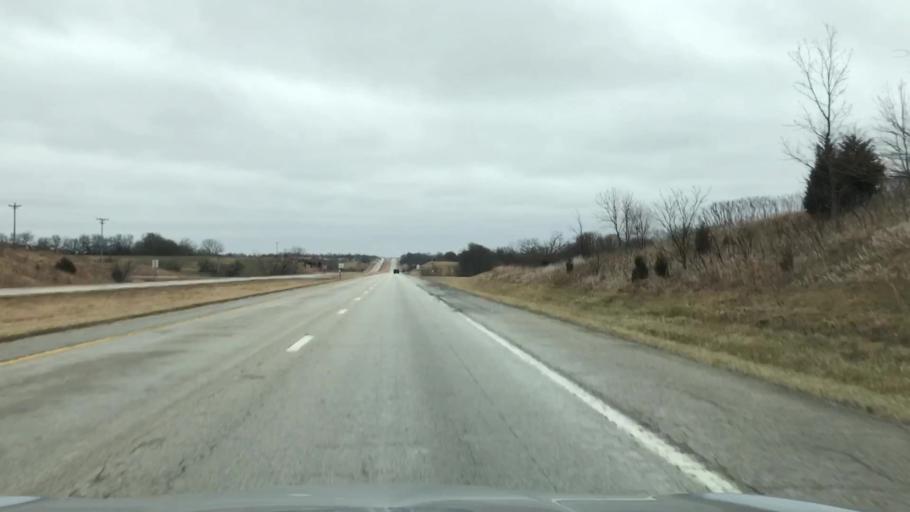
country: US
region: Missouri
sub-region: Clinton County
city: Cameron
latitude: 39.7507
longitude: -94.1319
